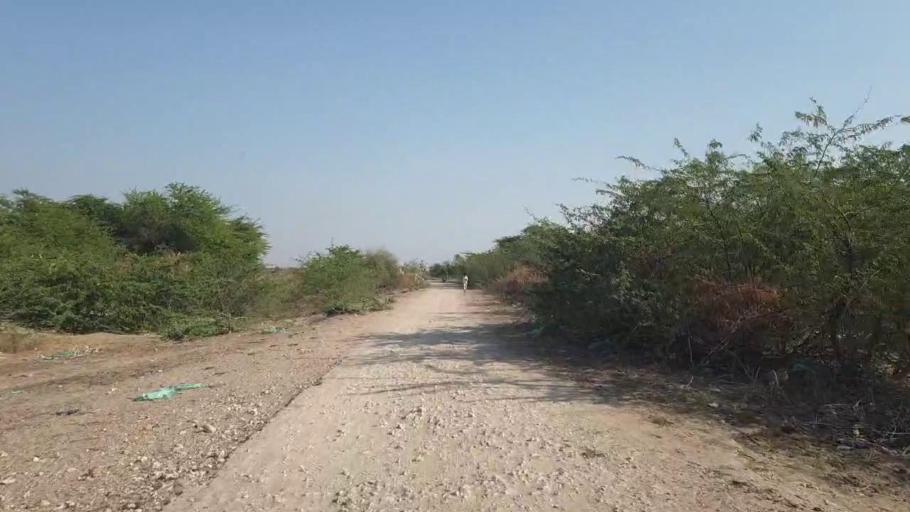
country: PK
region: Sindh
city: Chor
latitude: 25.5145
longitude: 69.6794
